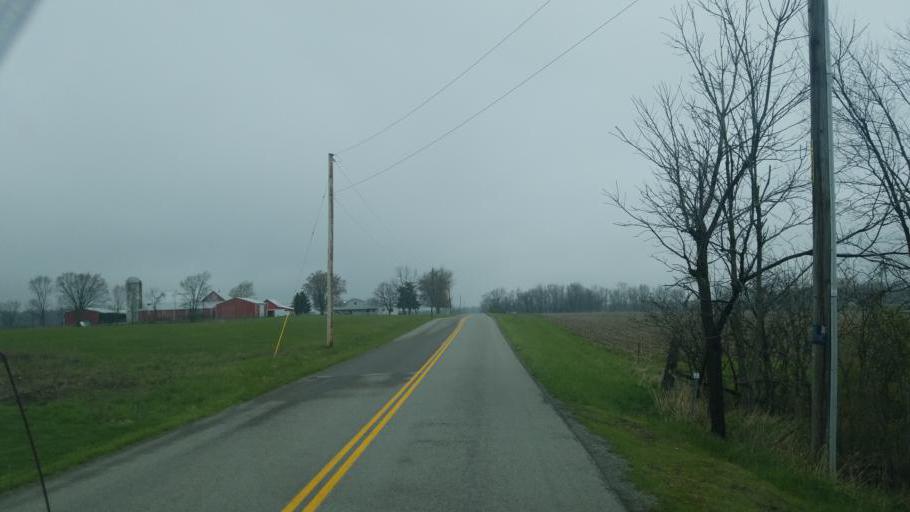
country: US
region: Ohio
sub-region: Logan County
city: Northwood
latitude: 40.4858
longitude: -83.6743
